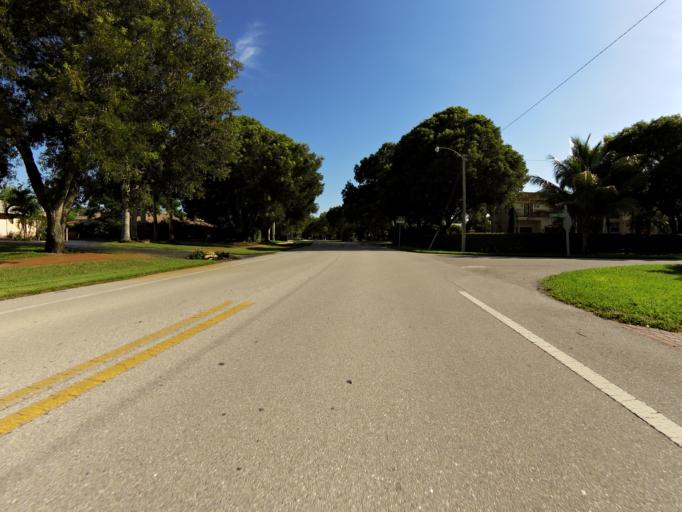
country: US
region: Florida
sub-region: Collier County
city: Naples
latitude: 26.1643
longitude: -81.8067
